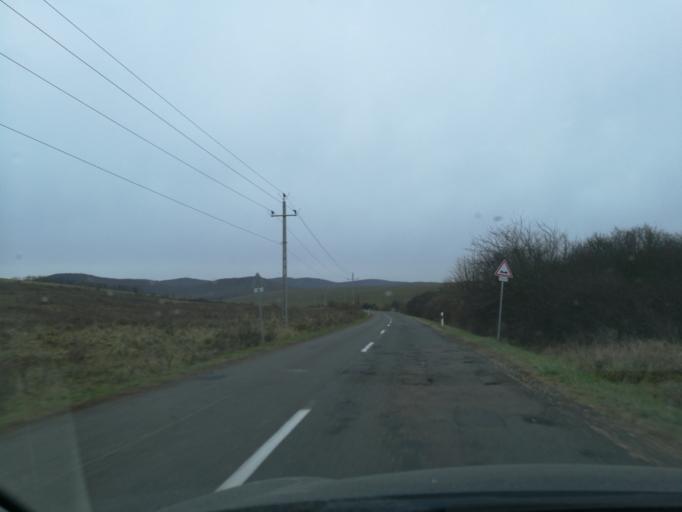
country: HU
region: Nograd
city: Rimoc
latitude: 48.0148
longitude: 19.5979
